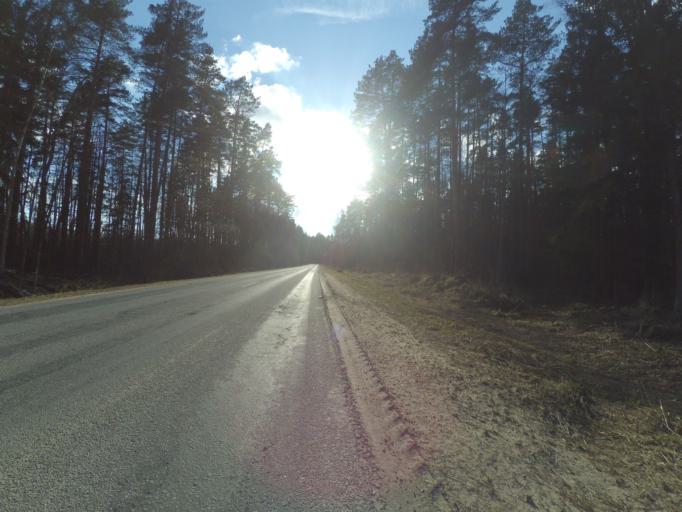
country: RU
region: Moskovskaya
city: Pushchino
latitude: 54.9045
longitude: 37.7086
